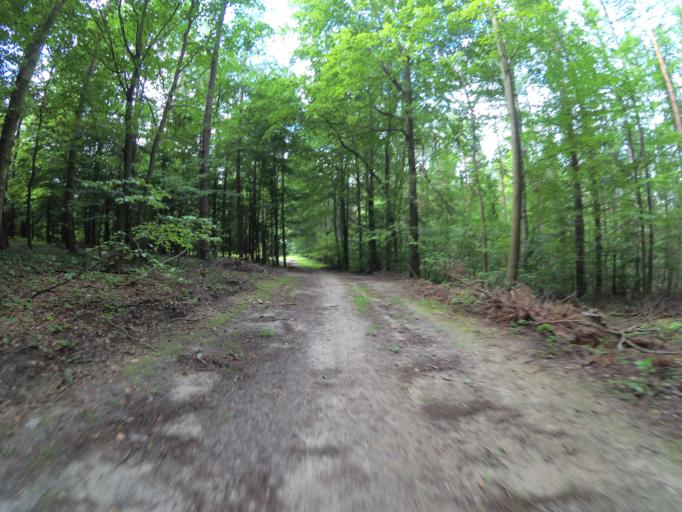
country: PL
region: Pomeranian Voivodeship
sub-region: Gdynia
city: Wielki Kack
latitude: 54.5048
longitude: 18.4477
